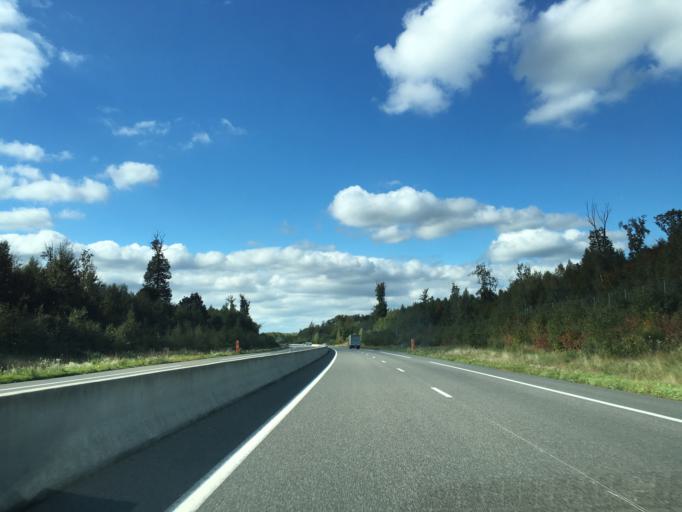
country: FR
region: Lorraine
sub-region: Departement de Meurthe-et-Moselle
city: Baccarat
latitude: 48.5094
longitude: 6.6690
